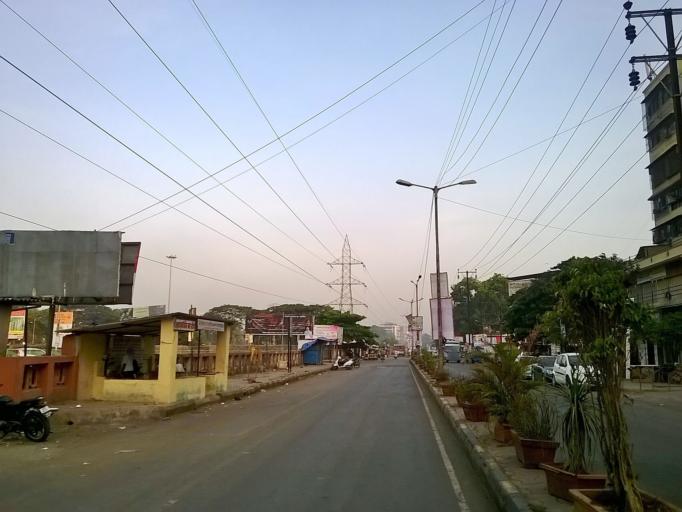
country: IN
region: Maharashtra
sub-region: Raigarh
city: Kalundri
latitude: 18.9914
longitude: 73.1234
